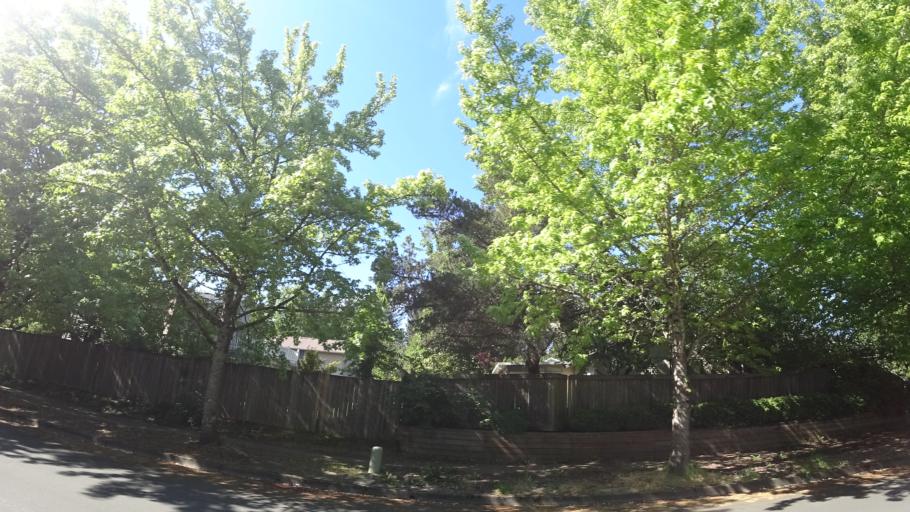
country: US
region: Oregon
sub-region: Washington County
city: Beaverton
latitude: 45.4476
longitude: -122.8153
